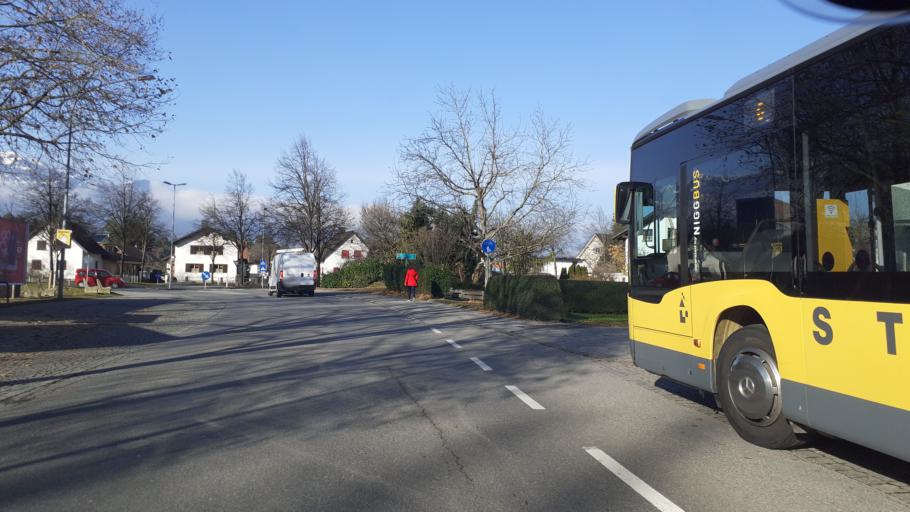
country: AT
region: Vorarlberg
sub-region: Politischer Bezirk Feldkirch
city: Nofels
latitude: 47.2546
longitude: 9.5864
